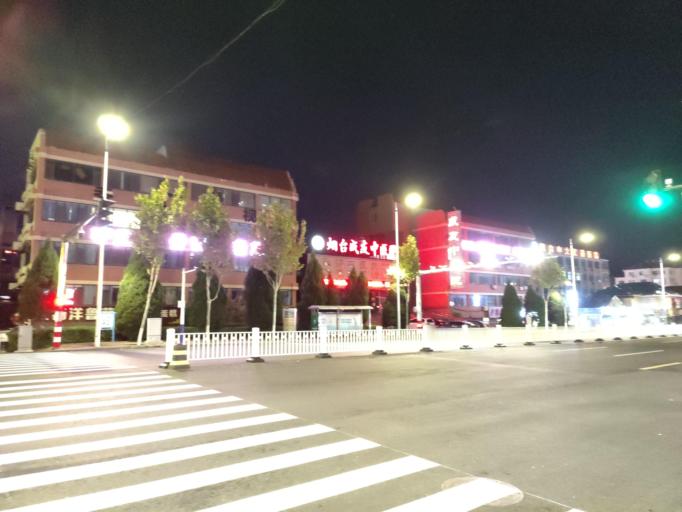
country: CN
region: Shandong Sheng
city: Xiangyang
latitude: 37.5196
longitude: 121.3913
